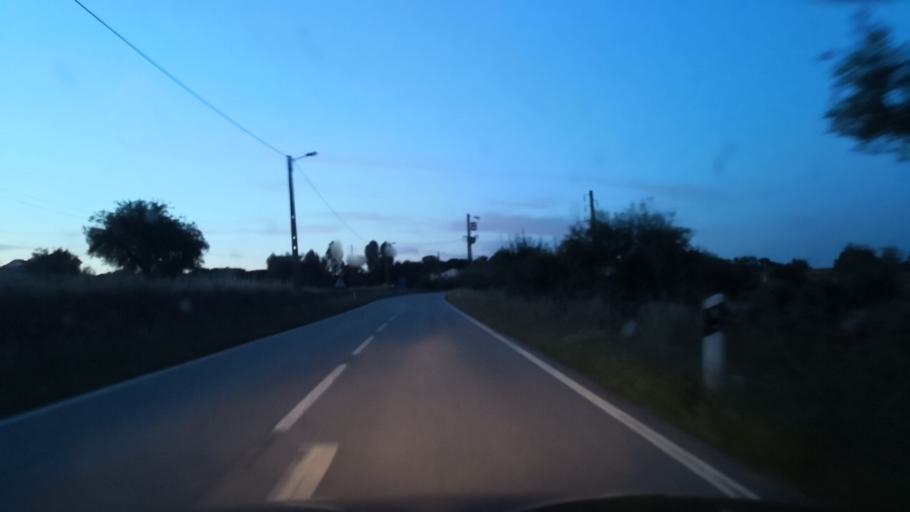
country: ES
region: Extremadura
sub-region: Provincia de Caceres
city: Piedras Albas
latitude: 39.8322
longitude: -6.9757
